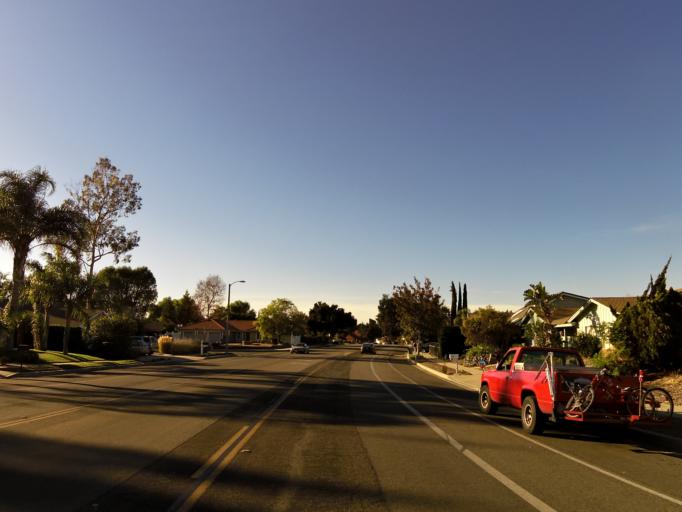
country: US
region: California
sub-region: Ventura County
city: Thousand Oaks
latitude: 34.2177
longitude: -118.8726
